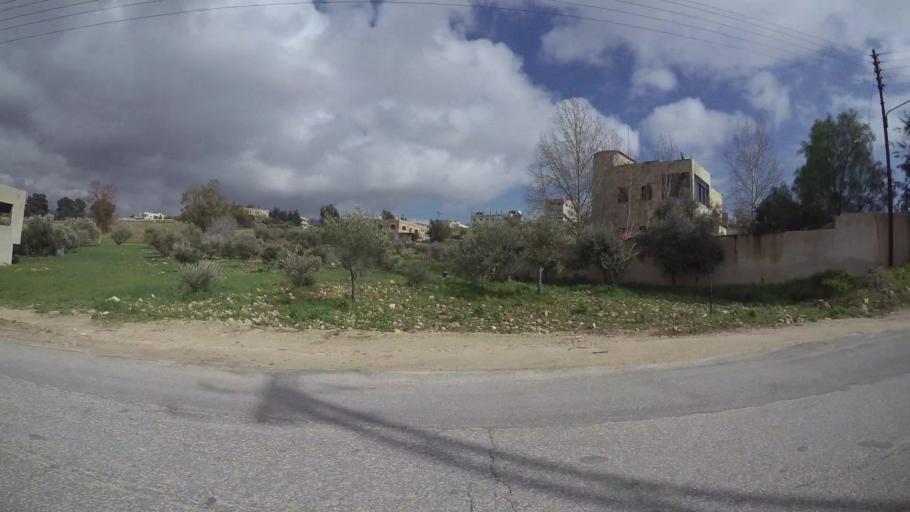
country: JO
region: Amman
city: Al Jubayhah
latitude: 32.0747
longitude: 35.8628
